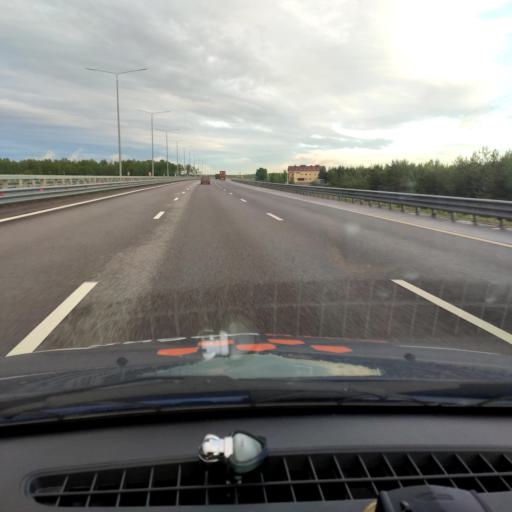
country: RU
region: Voronezj
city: Somovo
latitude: 51.7824
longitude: 39.2907
